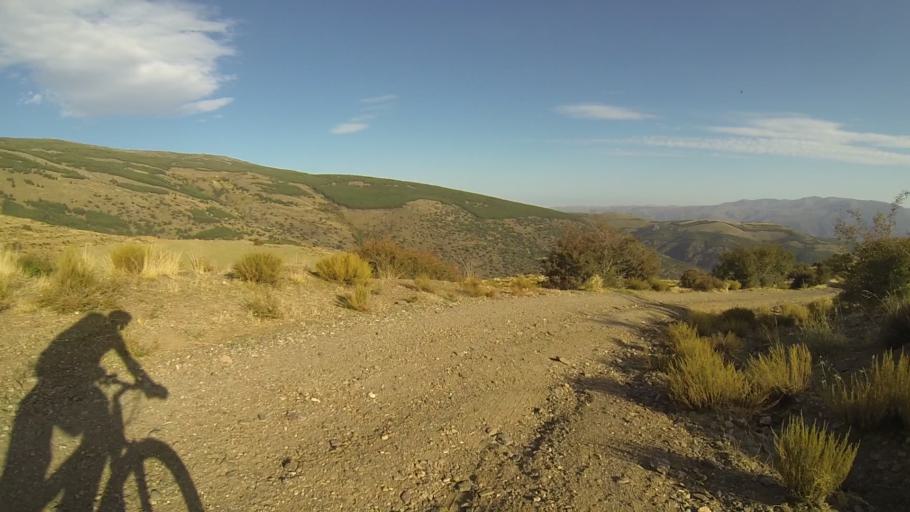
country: ES
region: Andalusia
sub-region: Provincia de Almeria
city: Laujar de Andarax
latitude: 37.0690
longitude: -2.8870
